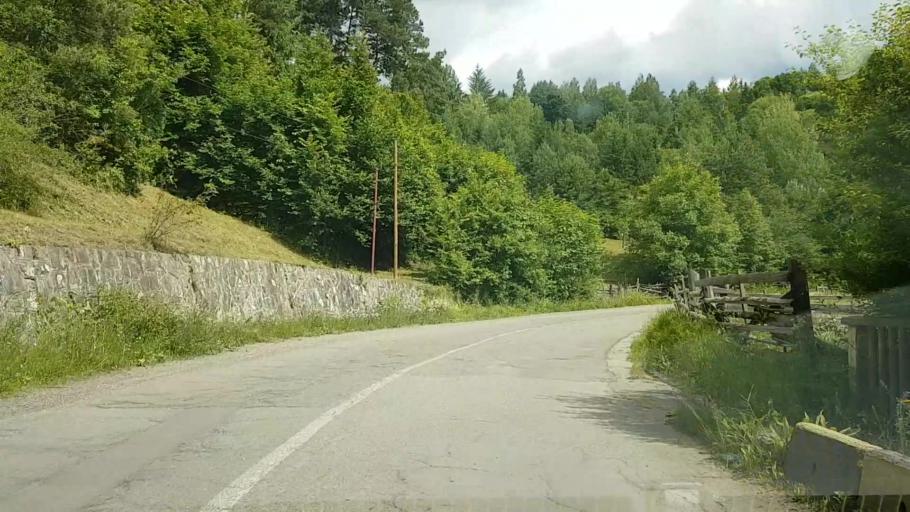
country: RO
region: Neamt
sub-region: Comuna Hangu
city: Hangu
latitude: 47.0511
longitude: 26.0406
